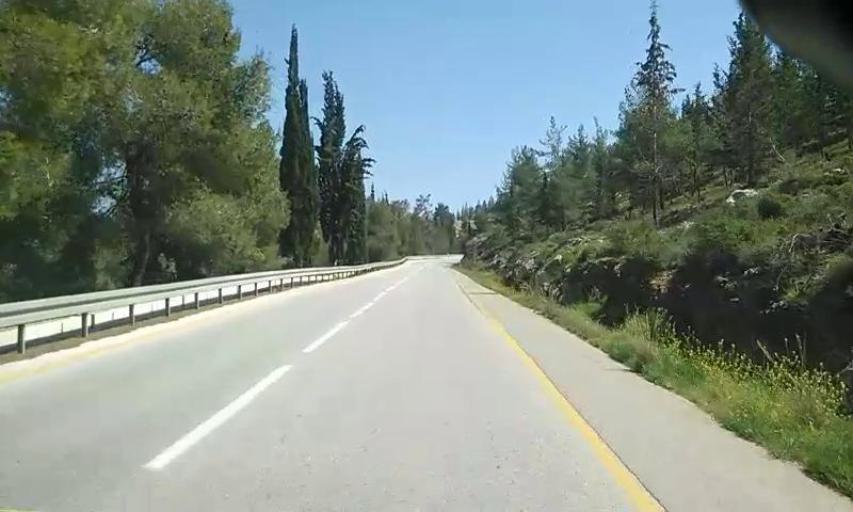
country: PS
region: West Bank
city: Nahhalin
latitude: 31.6737
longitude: 35.1025
